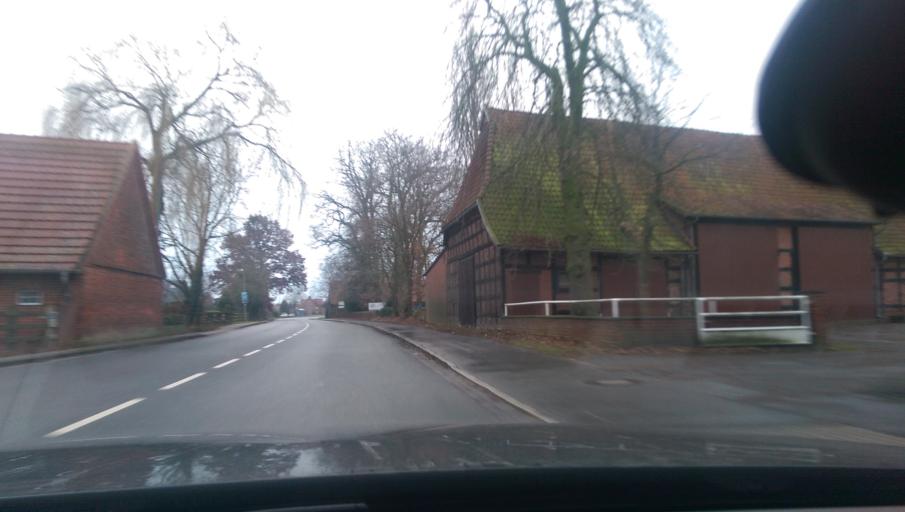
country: DE
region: Lower Saxony
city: Dorverden
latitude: 52.8547
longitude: 9.2363
